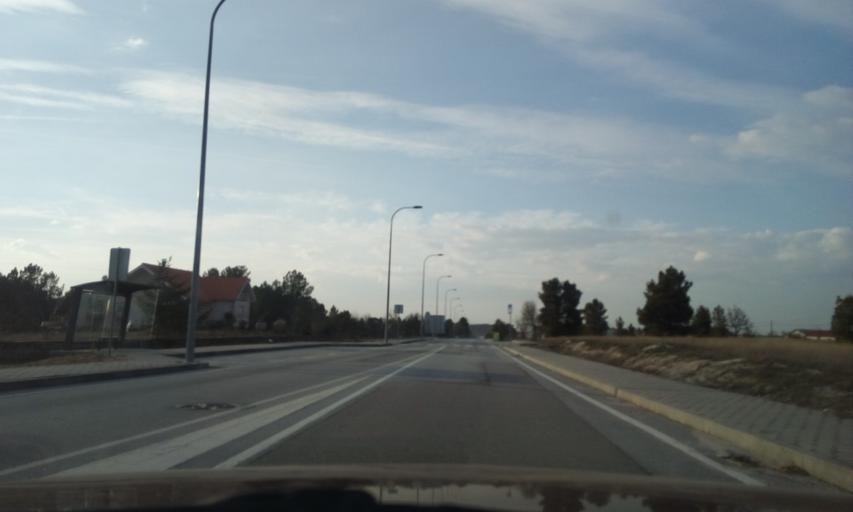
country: ES
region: Castille and Leon
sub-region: Provincia de Salamanca
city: Fuentes de Onoro
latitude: 40.5961
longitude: -6.9936
